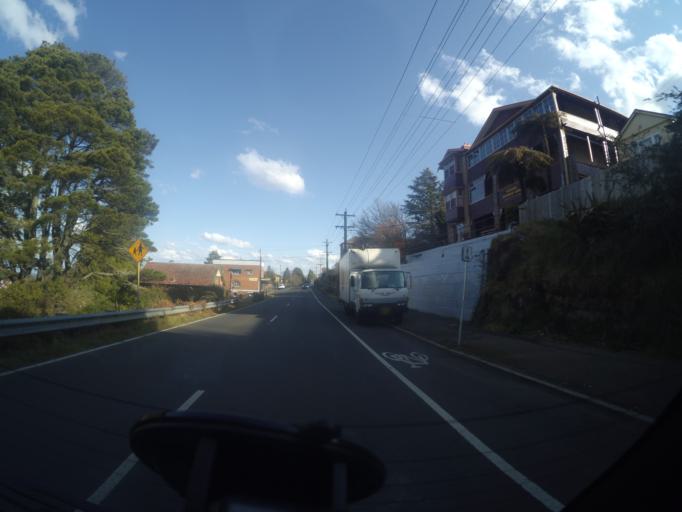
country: AU
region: New South Wales
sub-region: Blue Mountains Municipality
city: Katoomba
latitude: -33.7148
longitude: 150.3127
